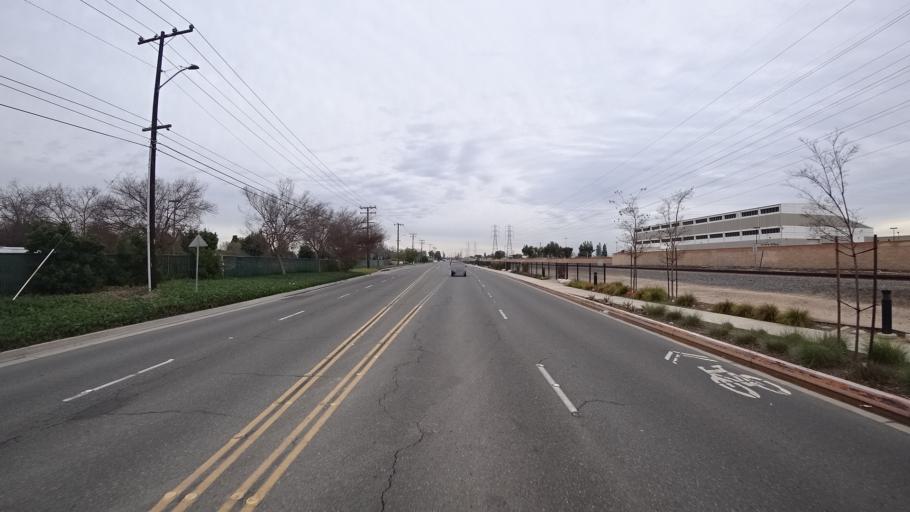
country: US
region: California
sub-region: Orange County
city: Midway City
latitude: 33.7484
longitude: -117.9984
